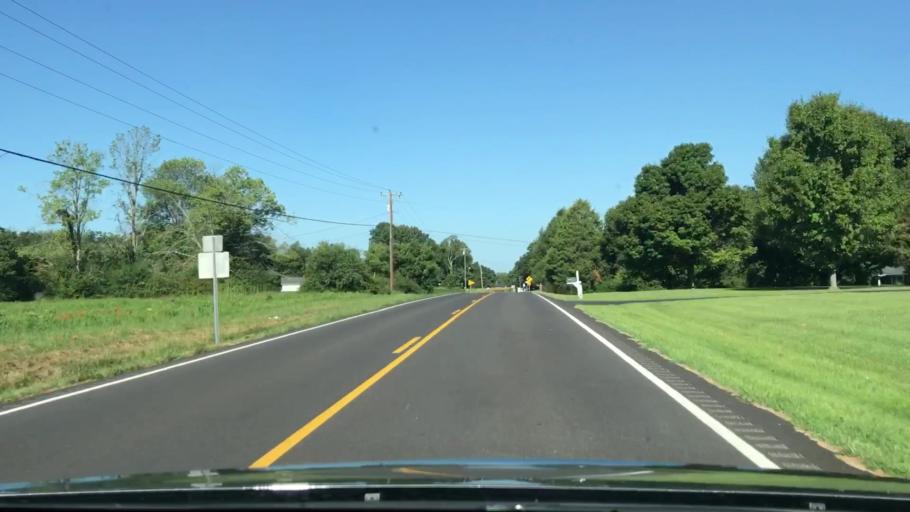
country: US
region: Kentucky
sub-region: Marshall County
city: Benton
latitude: 36.7677
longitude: -88.4333
